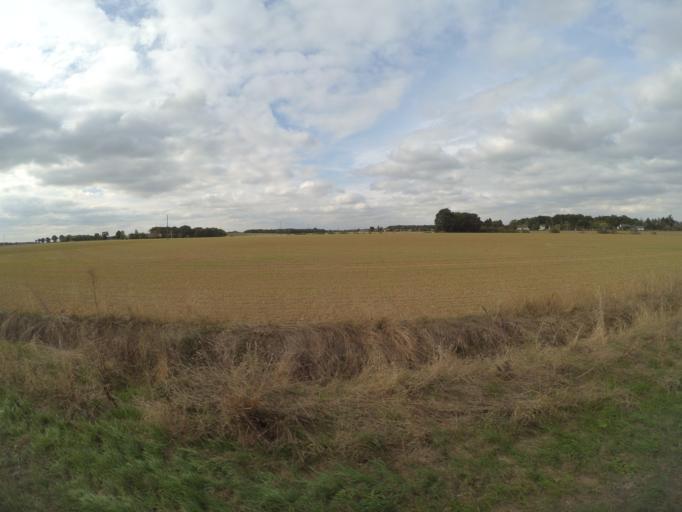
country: FR
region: Centre
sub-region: Departement d'Indre-et-Loire
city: Nazelles-Negron
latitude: 47.4818
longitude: 0.9445
